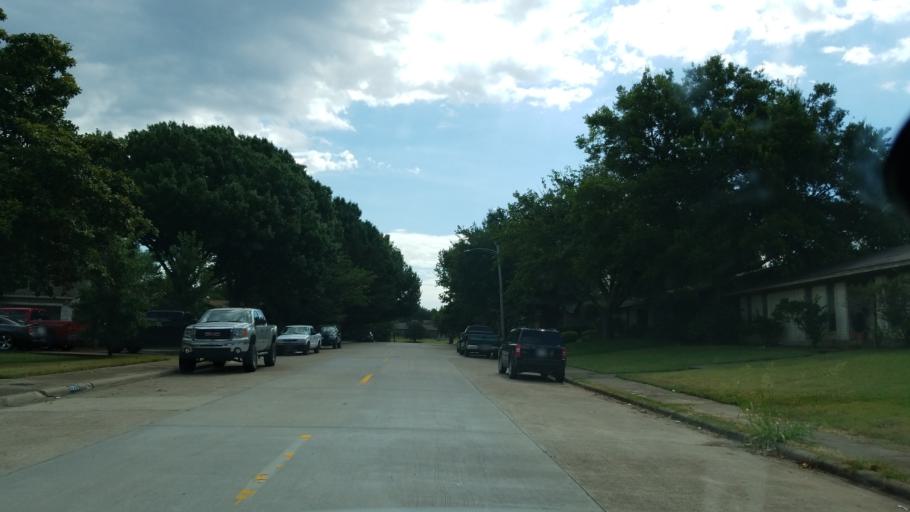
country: US
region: Texas
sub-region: Dallas County
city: Duncanville
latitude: 32.6545
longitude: -96.8435
